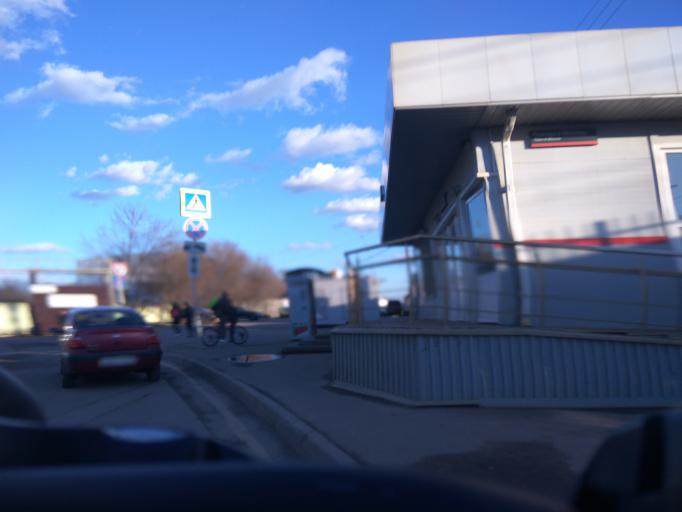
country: RU
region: Moscow
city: Ostankinskiy
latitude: 55.8181
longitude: 37.6030
